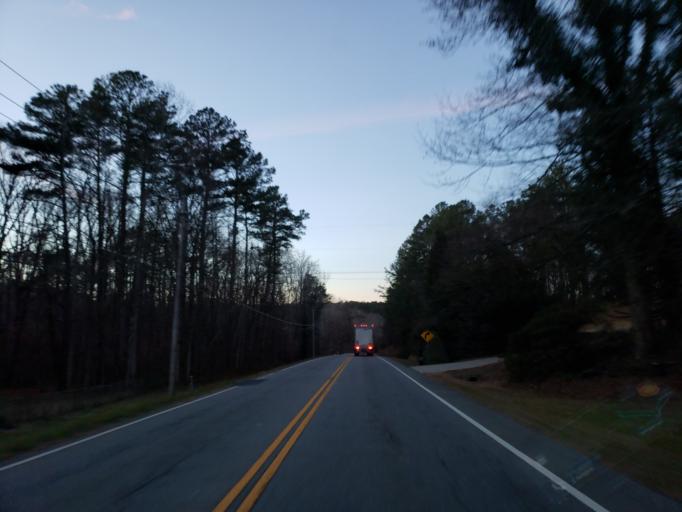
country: US
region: Georgia
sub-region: Paulding County
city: Hiram
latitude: 33.9553
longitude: -84.7058
